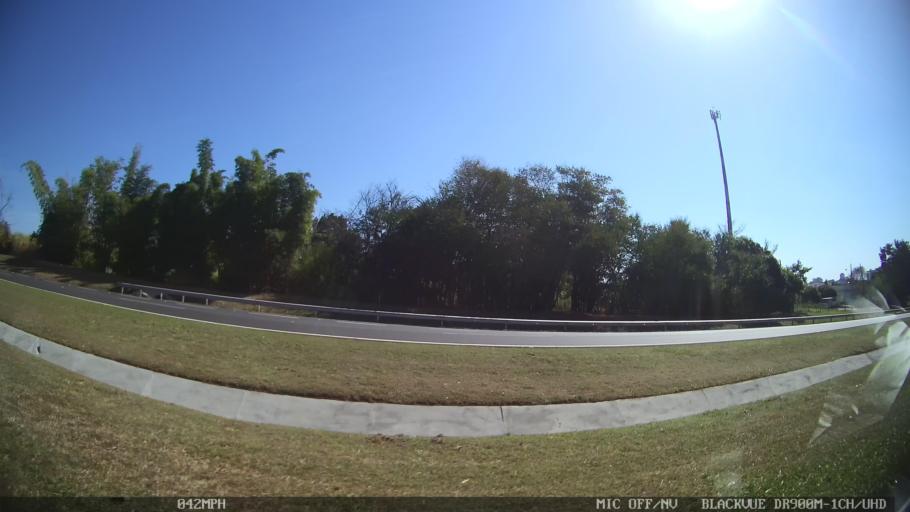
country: BR
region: Sao Paulo
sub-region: Ribeirao Preto
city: Ribeirao Preto
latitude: -21.2208
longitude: -47.7757
